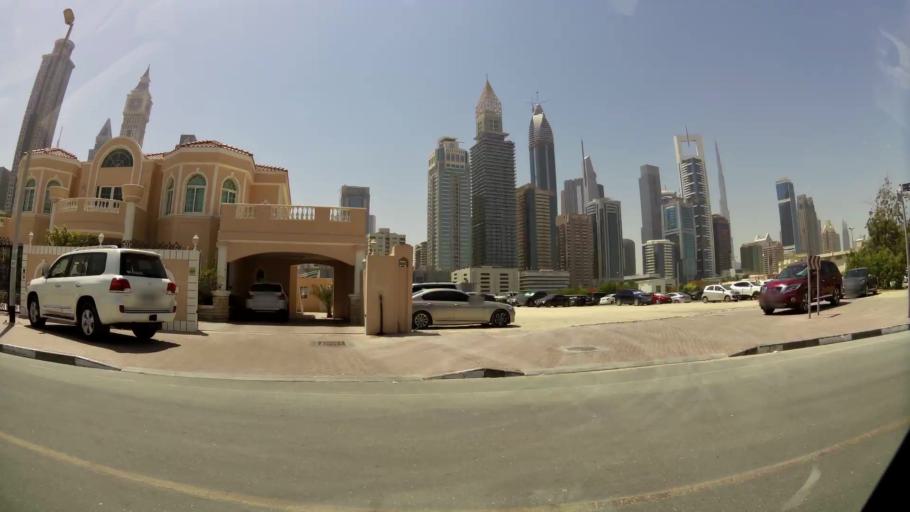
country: AE
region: Dubai
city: Dubai
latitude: 25.2173
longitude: 55.2737
